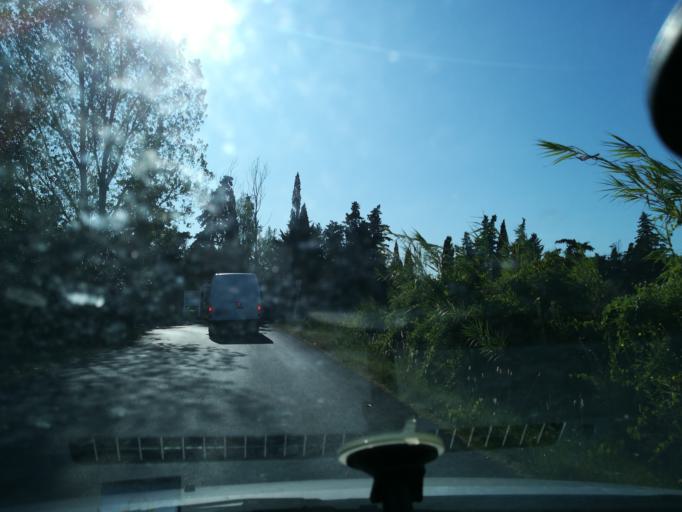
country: FR
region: Languedoc-Roussillon
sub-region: Departement de l'Herault
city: Vias
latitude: 43.2910
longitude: 3.3819
